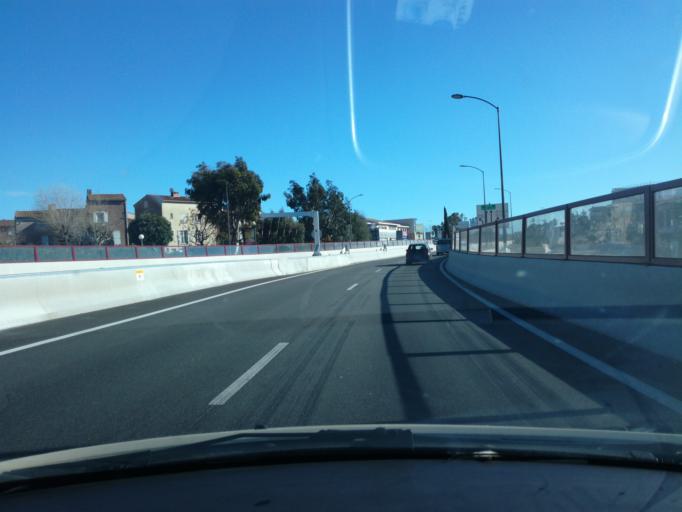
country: FR
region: Provence-Alpes-Cote d'Azur
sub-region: Departement du Var
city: Puget-sur-Argens
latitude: 43.4548
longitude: 6.6905
